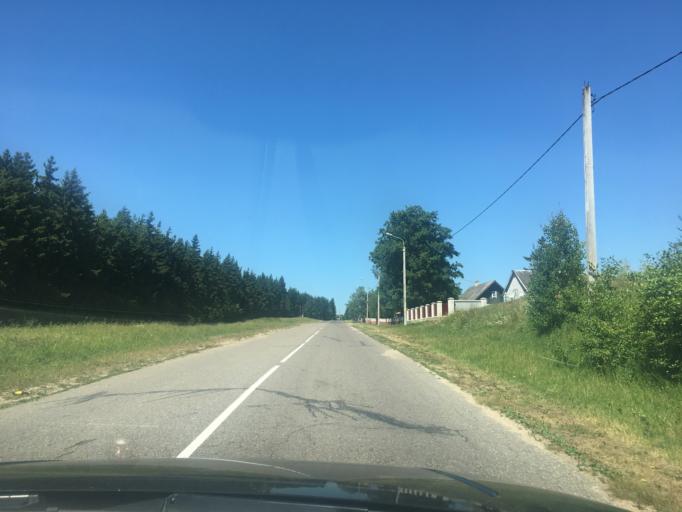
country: BY
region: Grodnenskaya
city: Hal'shany
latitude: 54.2623
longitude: 25.9951
